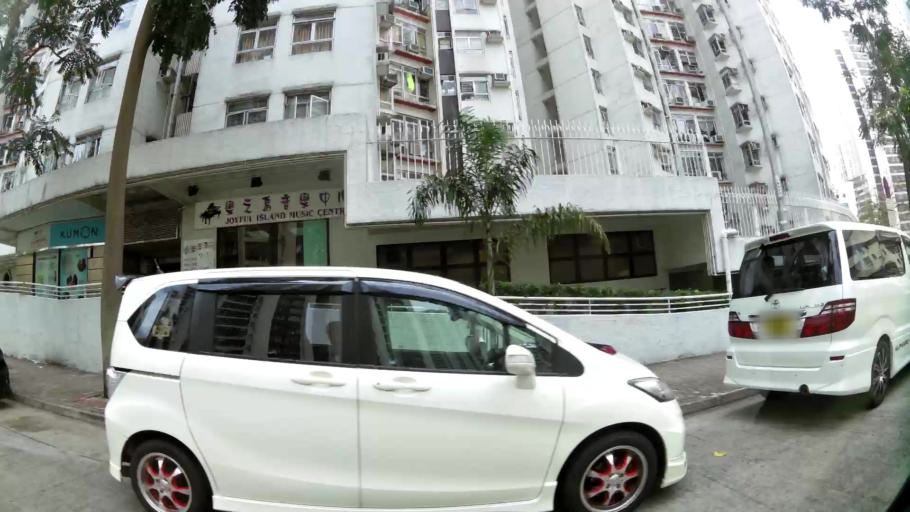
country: HK
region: Wanchai
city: Wan Chai
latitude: 22.2856
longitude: 114.2155
